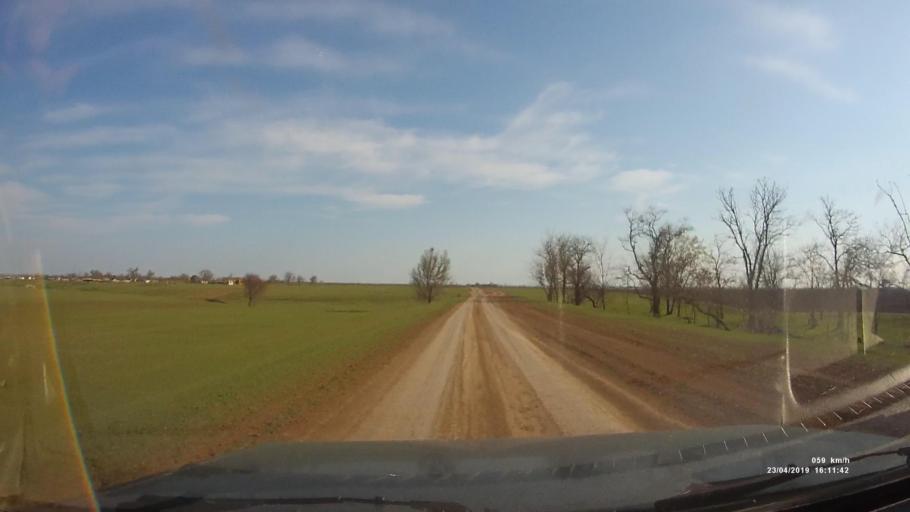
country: RU
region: Rostov
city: Remontnoye
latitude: 46.4732
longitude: 43.1226
